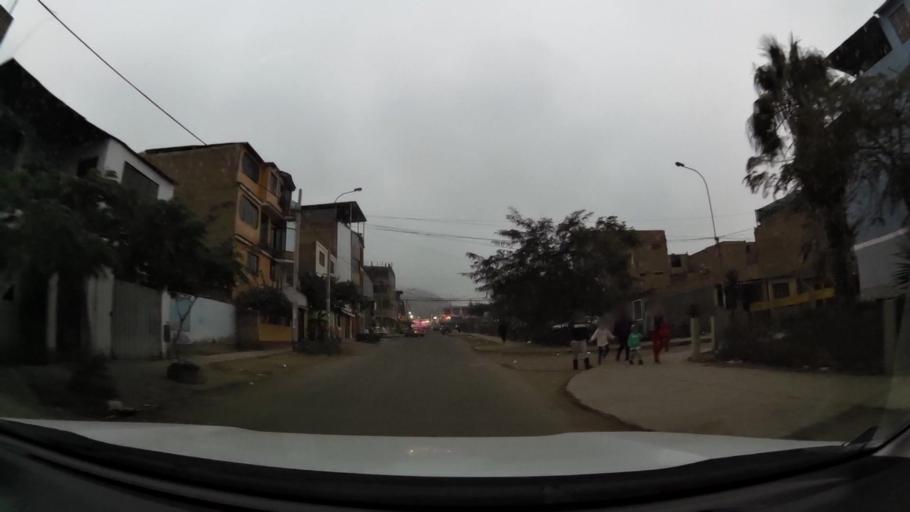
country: PE
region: Lima
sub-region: Lima
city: Surco
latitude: -12.1482
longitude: -76.9713
